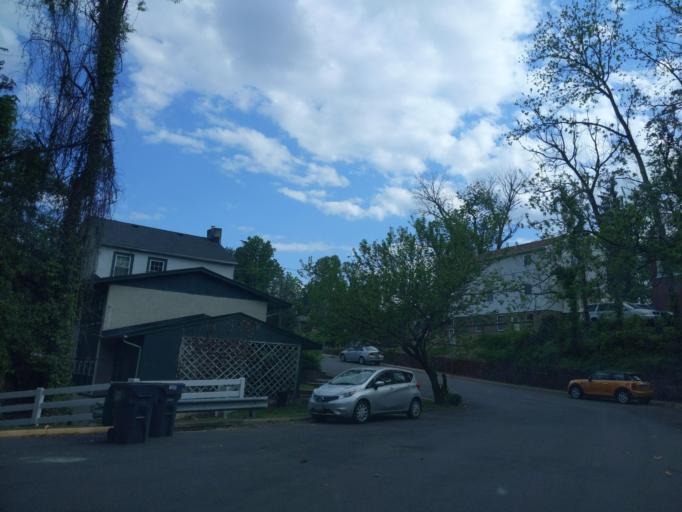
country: US
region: Virginia
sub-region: City of Charlottesville
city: Charlottesville
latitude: 38.0276
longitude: -78.5126
